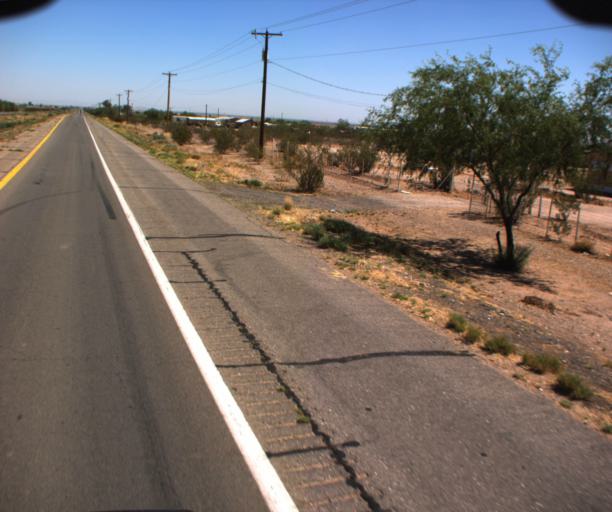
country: US
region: Arizona
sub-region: Pinal County
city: Maricopa
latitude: 32.8827
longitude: -112.0493
